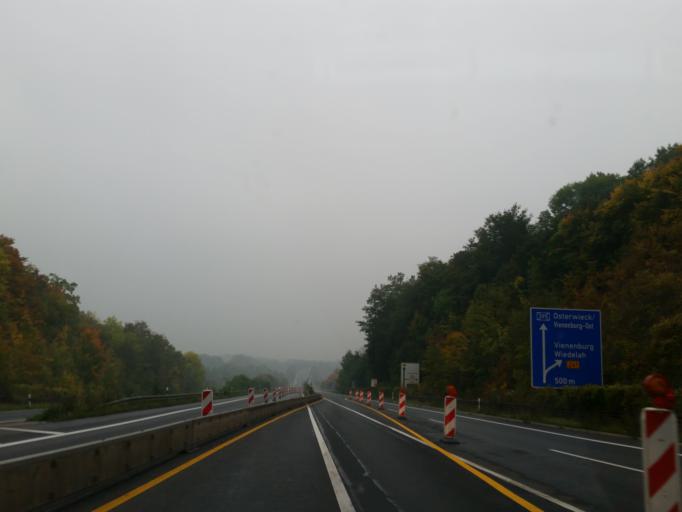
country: DE
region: Lower Saxony
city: Vienenburg
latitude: 51.9631
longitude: 10.5760
